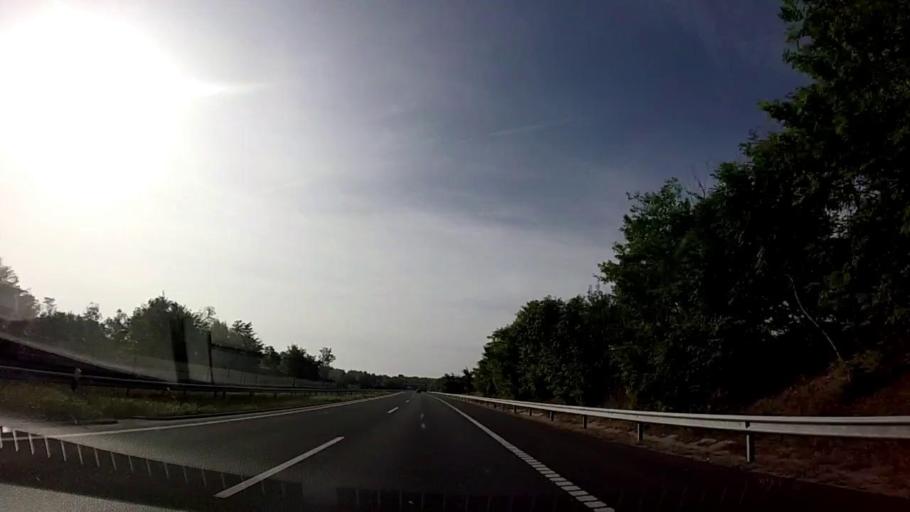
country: HU
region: Somogy
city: Balatonfoldvar
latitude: 46.8253
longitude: 17.9318
